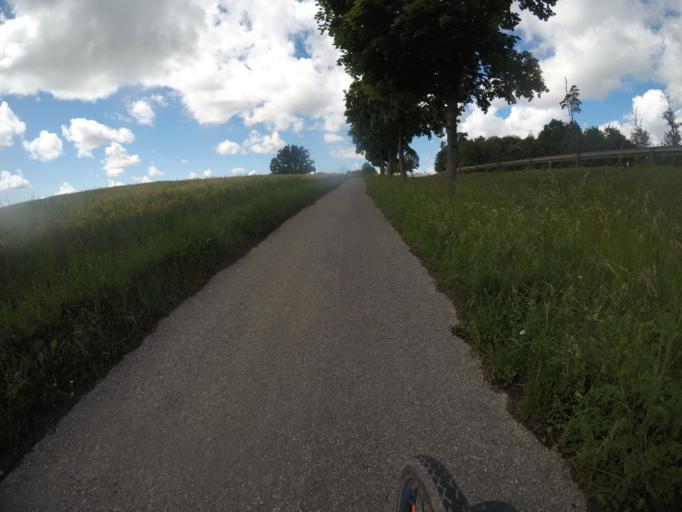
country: DE
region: Baden-Wuerttemberg
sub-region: Regierungsbezirk Stuttgart
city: Motzingen
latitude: 48.5461
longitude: 8.7803
